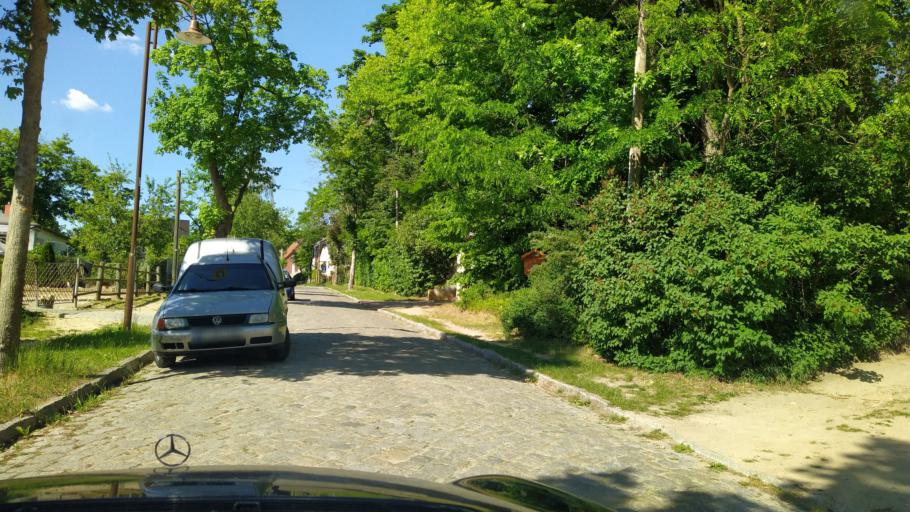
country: DE
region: Brandenburg
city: Trebbin
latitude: 52.2491
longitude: 13.2567
